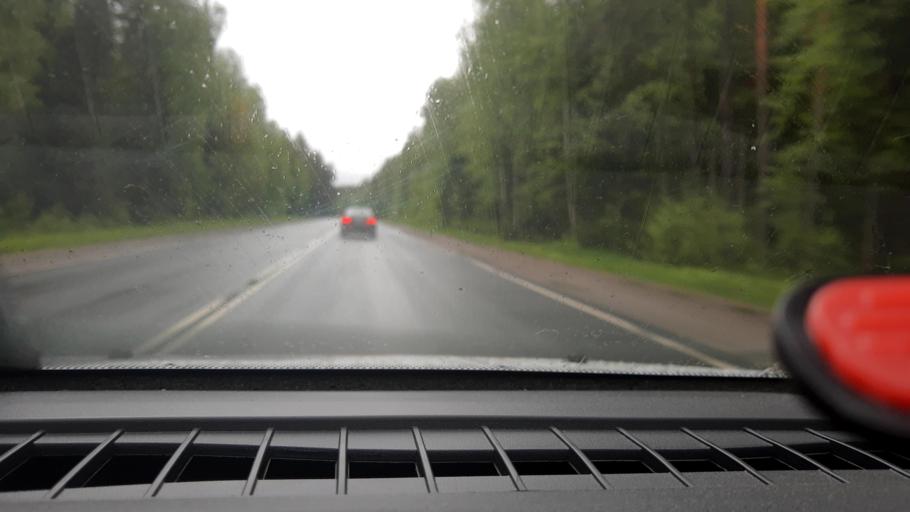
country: RU
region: Nizjnij Novgorod
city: Semenov
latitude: 56.7405
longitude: 44.3407
